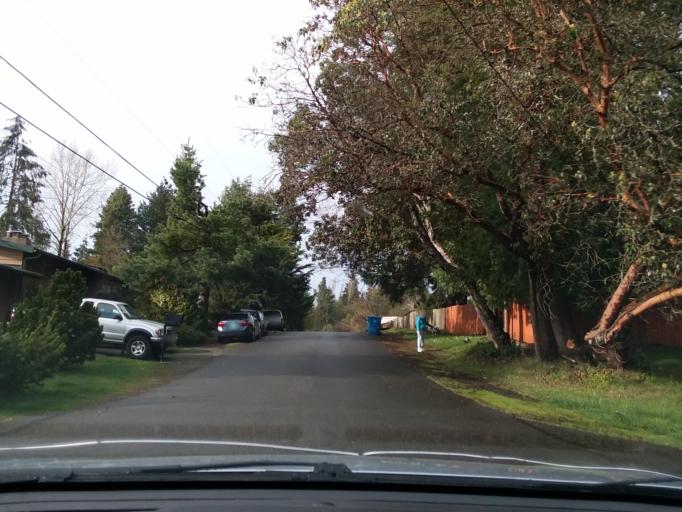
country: US
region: Washington
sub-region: King County
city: Shoreline
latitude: 47.7445
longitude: -122.3265
